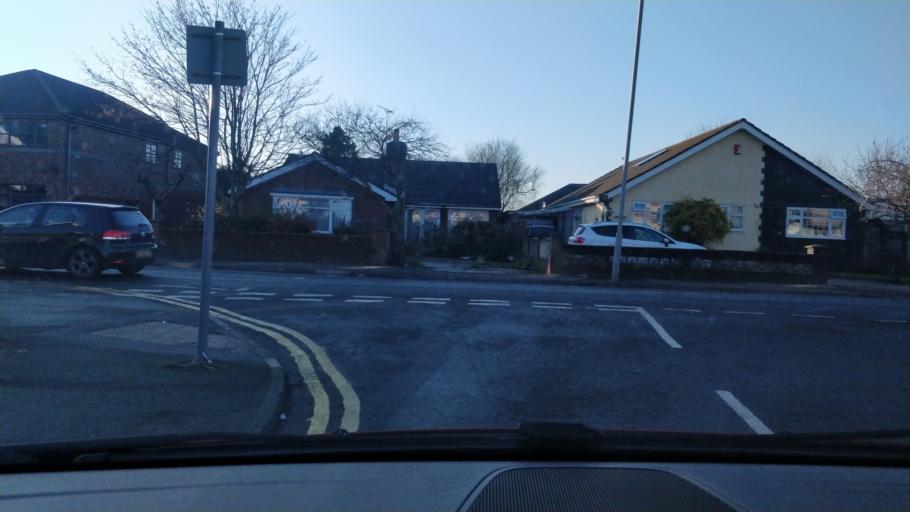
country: GB
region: England
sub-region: Lancashire
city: Banks
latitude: 53.6721
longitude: -2.9482
